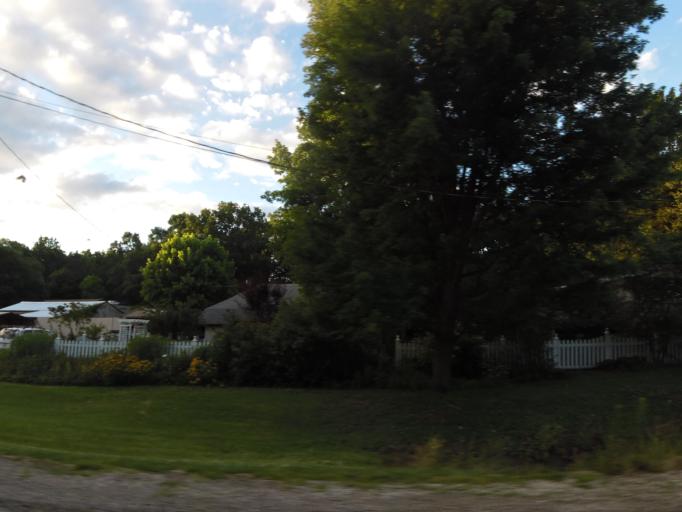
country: US
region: Missouri
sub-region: Jefferson County
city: Cedar Hill
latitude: 38.3341
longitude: -90.6719
